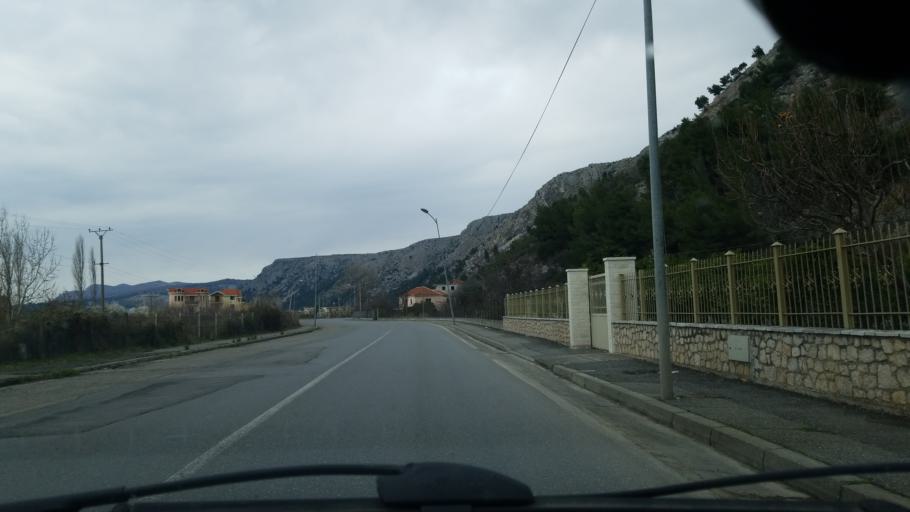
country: AL
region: Lezhe
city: Lezhe
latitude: 41.7923
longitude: 19.6230
